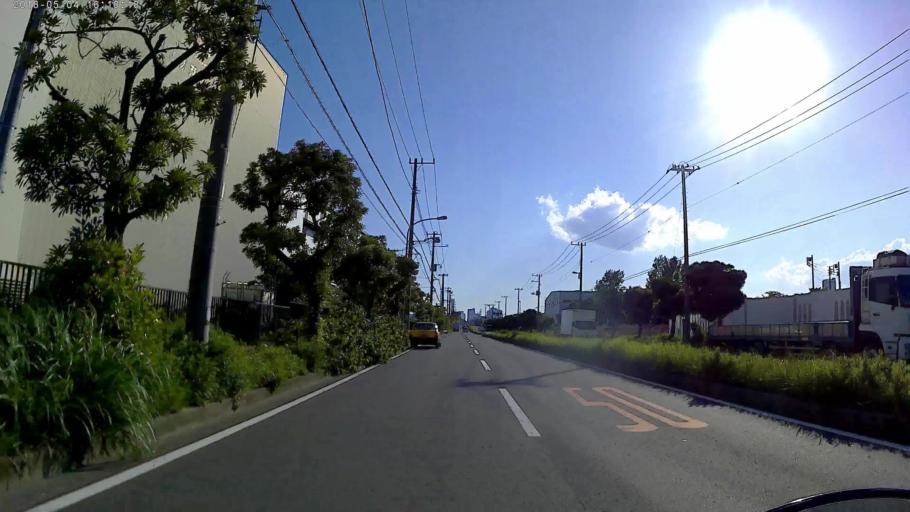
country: JP
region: Kanagawa
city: Yokohama
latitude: 35.4852
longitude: 139.6703
